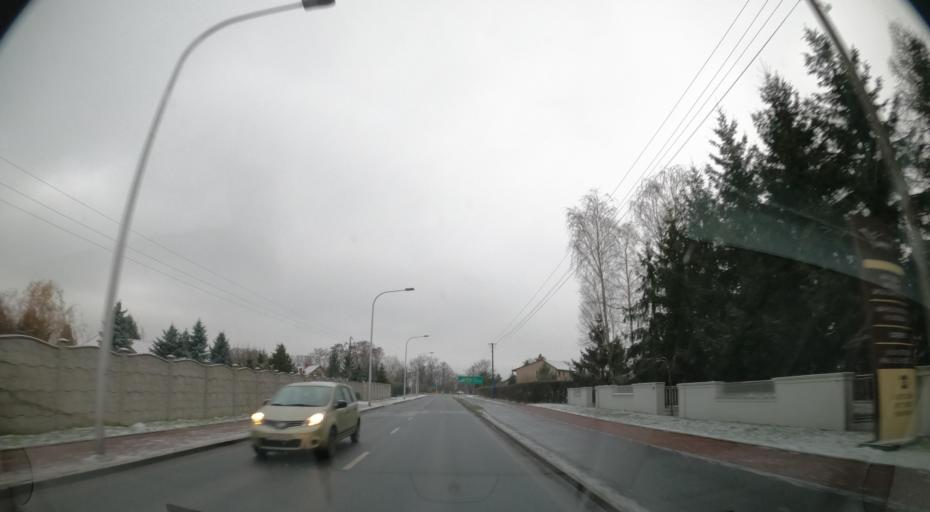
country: PL
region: Masovian Voivodeship
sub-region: Powiat plocki
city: Maszewo Duze
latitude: 52.5614
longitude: 19.6427
